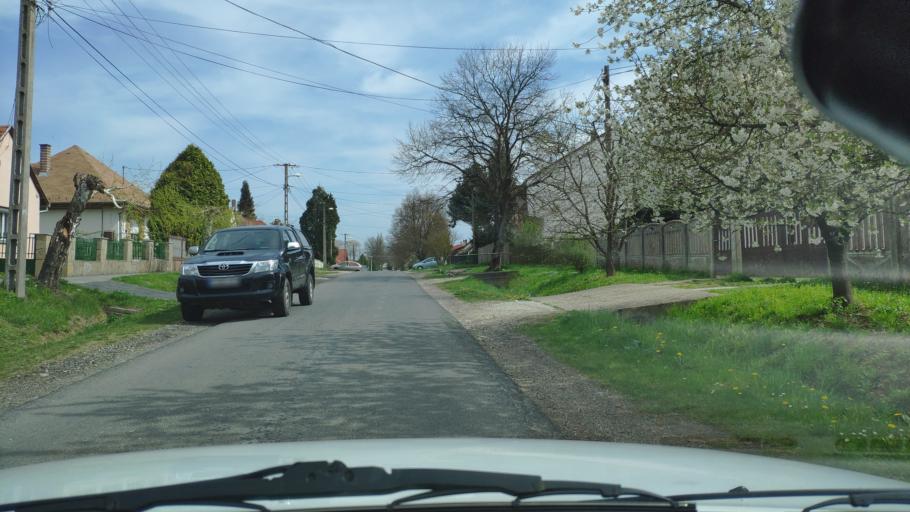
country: HU
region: Zala
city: Nagykanizsa
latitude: 46.4181
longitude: 16.9932
